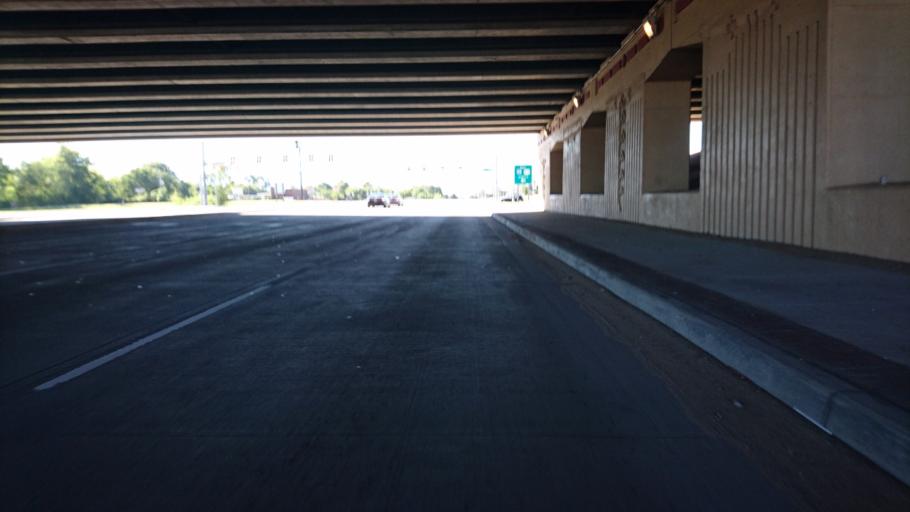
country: US
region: Oklahoma
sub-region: Rogers County
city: Catoosa
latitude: 36.1628
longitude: -95.7617
